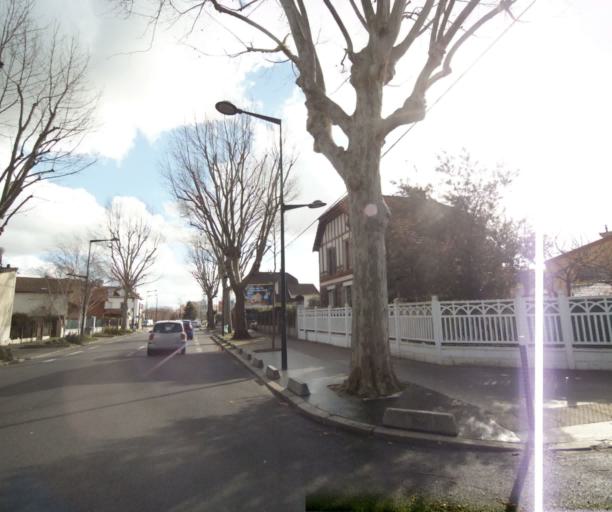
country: FR
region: Ile-de-France
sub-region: Departement de Seine-Saint-Denis
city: Villetaneuse
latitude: 48.9500
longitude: 2.3411
